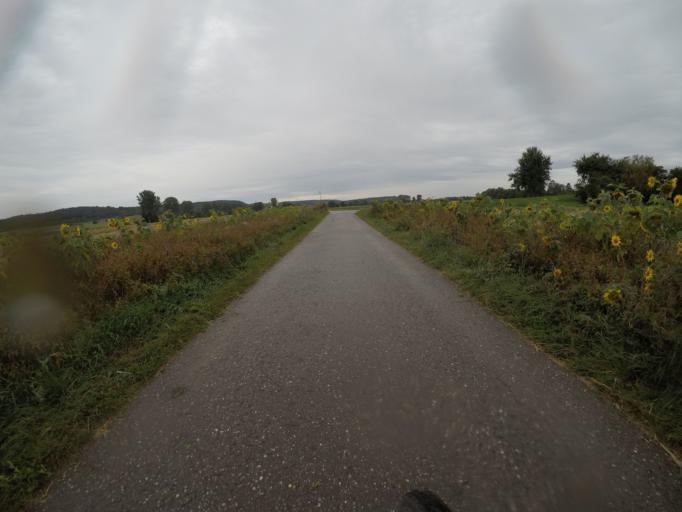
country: DE
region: Baden-Wuerttemberg
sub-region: Regierungsbezirk Stuttgart
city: Ehningen
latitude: 48.6394
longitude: 8.9317
